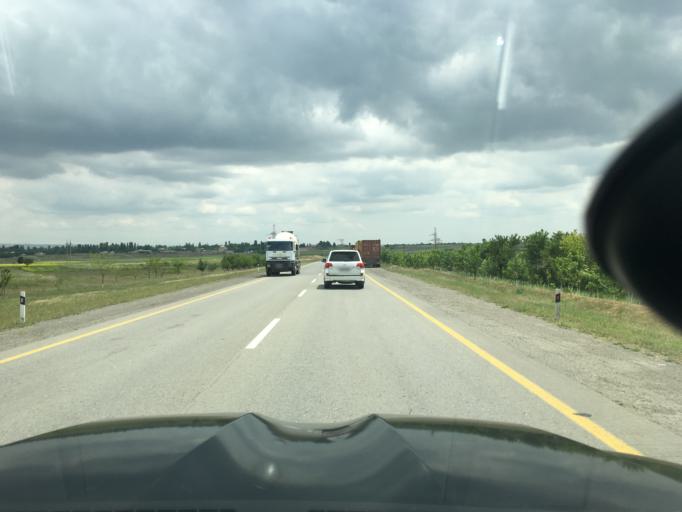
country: AZ
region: Tovuz
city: Qaraxanli
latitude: 41.0295
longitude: 45.6097
